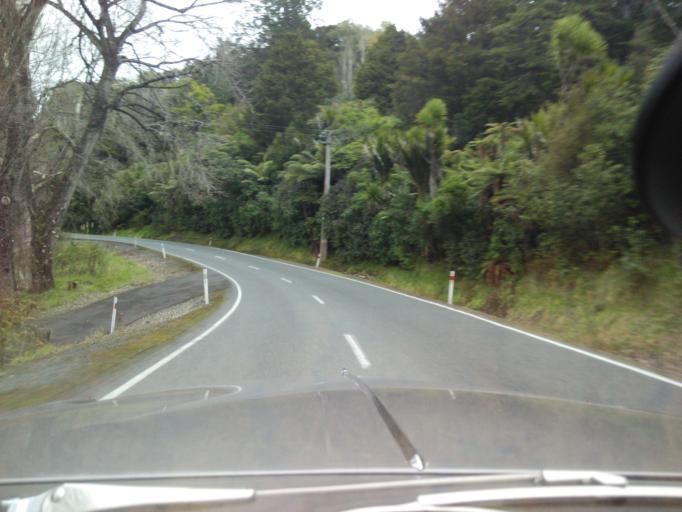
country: NZ
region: Auckland
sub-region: Auckland
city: Warkworth
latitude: -36.5043
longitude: 174.6444
